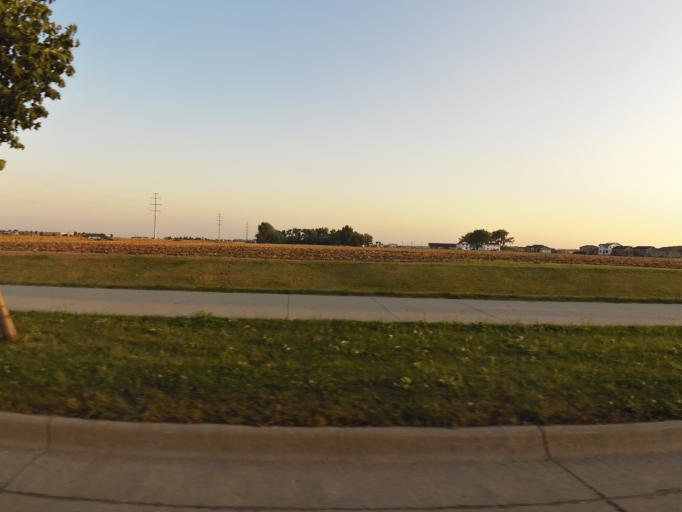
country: US
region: North Dakota
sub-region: Grand Forks County
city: Grand Forks
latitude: 47.8822
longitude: -97.0684
